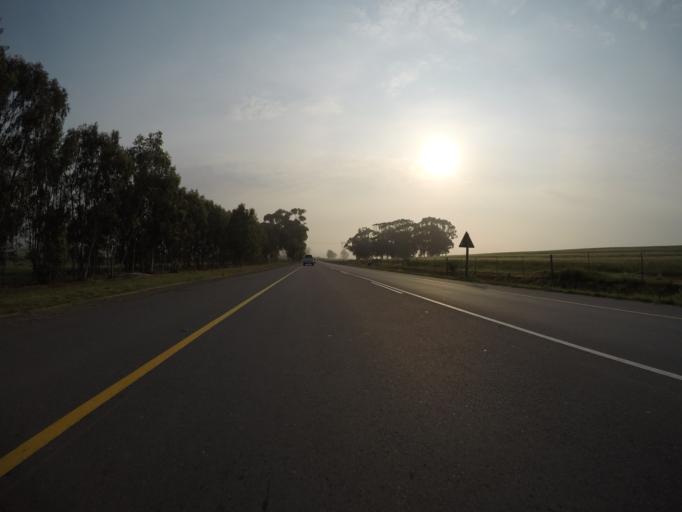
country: ZA
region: Western Cape
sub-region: City of Cape Town
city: Kraaifontein
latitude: -33.8058
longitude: 18.6787
